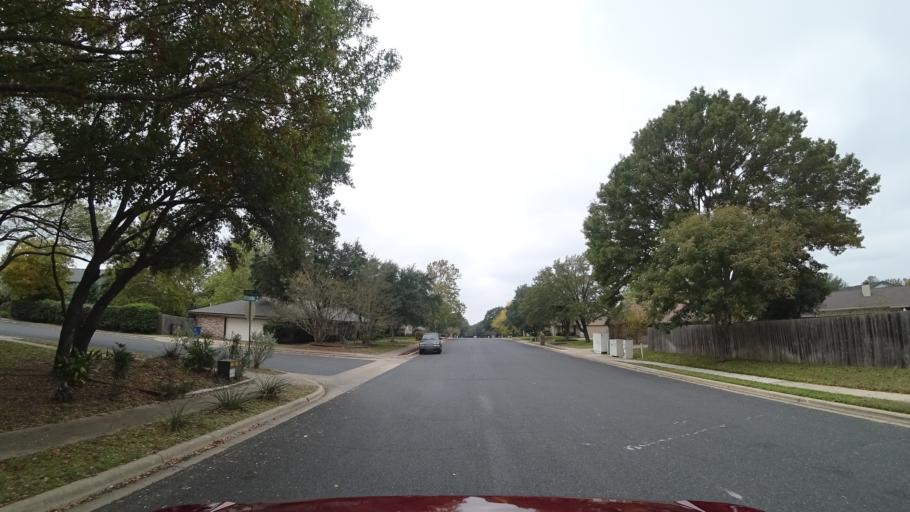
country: US
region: Texas
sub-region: Williamson County
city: Anderson Mill
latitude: 30.4461
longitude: -97.8111
